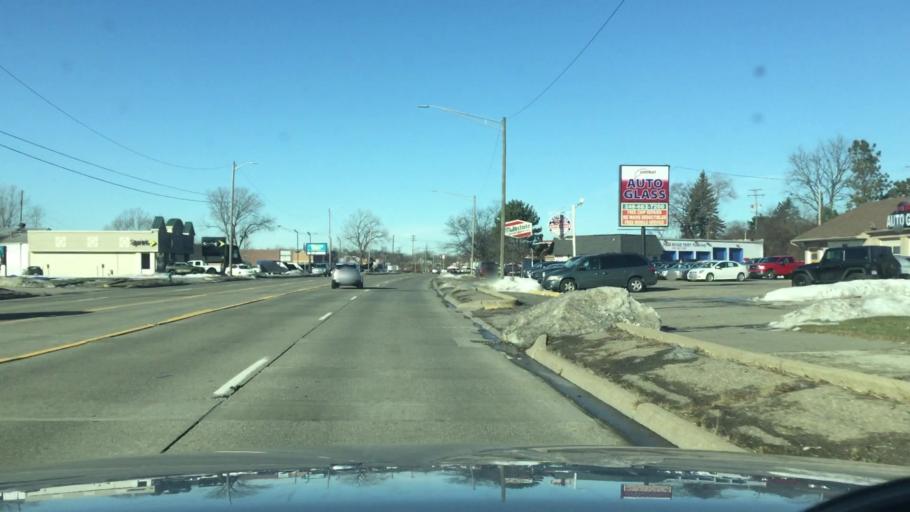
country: US
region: Michigan
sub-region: Oakland County
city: Keego Harbor
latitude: 42.6372
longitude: -83.3483
